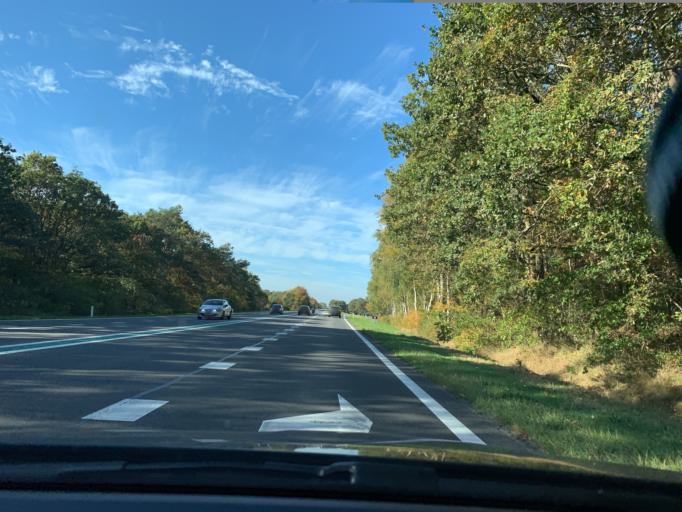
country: NL
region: Drenthe
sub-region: Gemeente Tynaarlo
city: Zuidlaren
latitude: 53.0827
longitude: 6.6600
